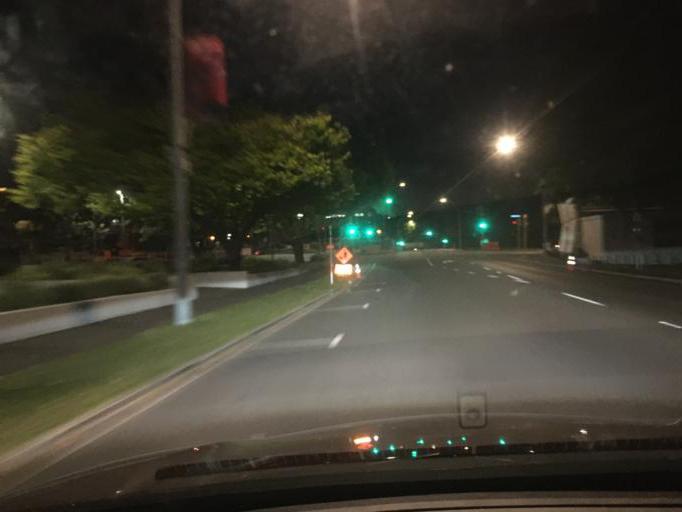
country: NZ
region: Waikato
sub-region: Hamilton City
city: Hamilton
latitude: -37.7870
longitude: 175.2759
